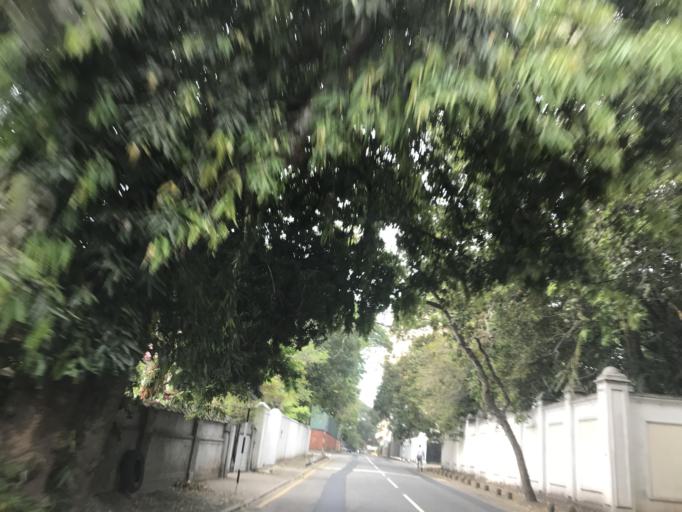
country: LK
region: Western
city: Colombo
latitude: 6.8993
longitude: 79.8580
